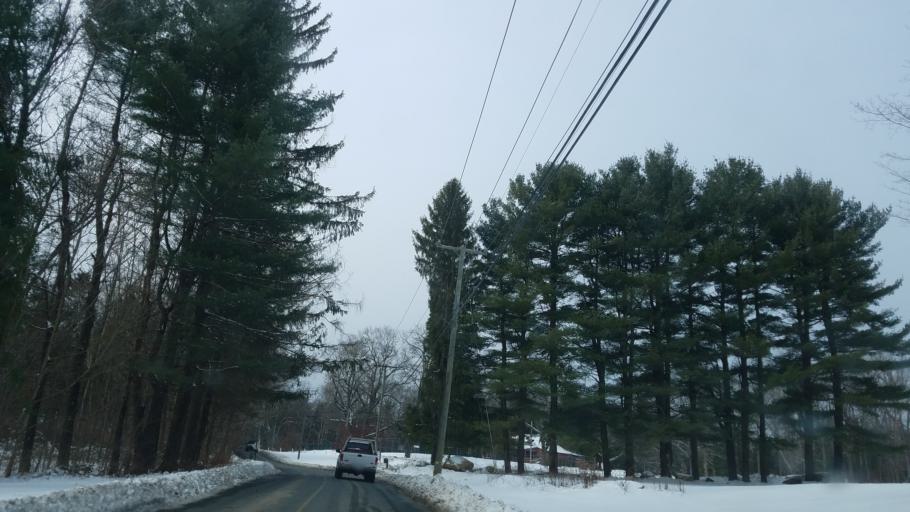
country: US
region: Connecticut
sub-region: Litchfield County
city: Winsted
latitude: 41.8727
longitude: -73.0341
